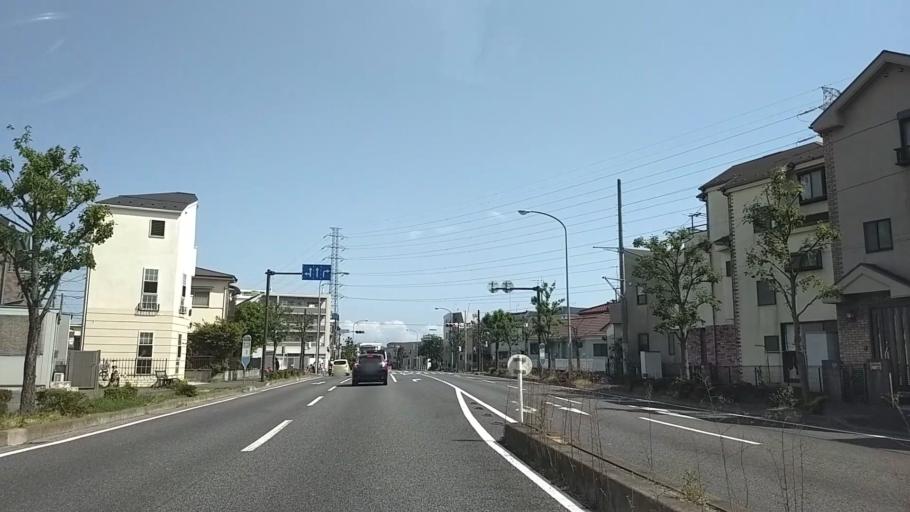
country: JP
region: Kanagawa
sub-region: Kawasaki-shi
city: Kawasaki
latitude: 35.5473
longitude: 139.6302
